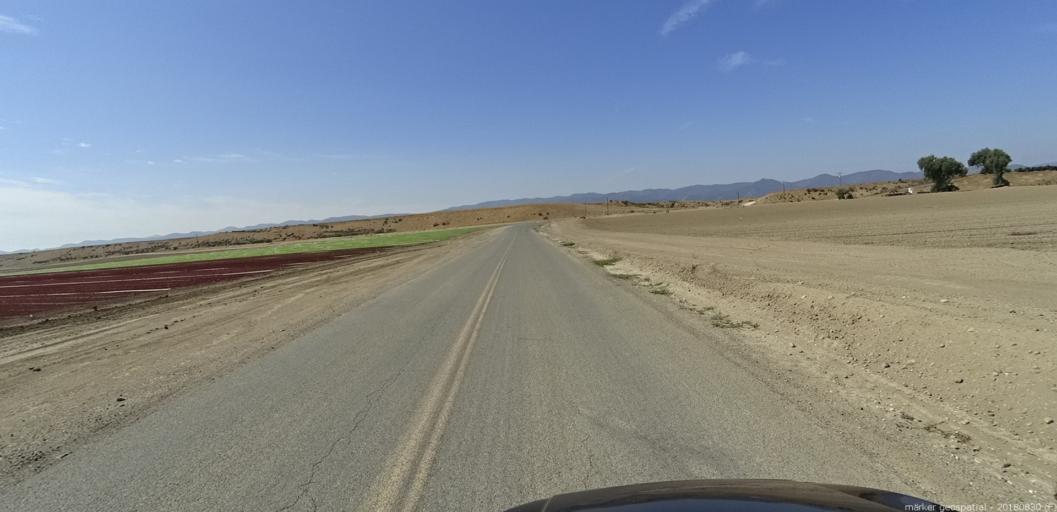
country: US
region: California
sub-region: Monterey County
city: King City
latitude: 36.1129
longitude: -121.0307
